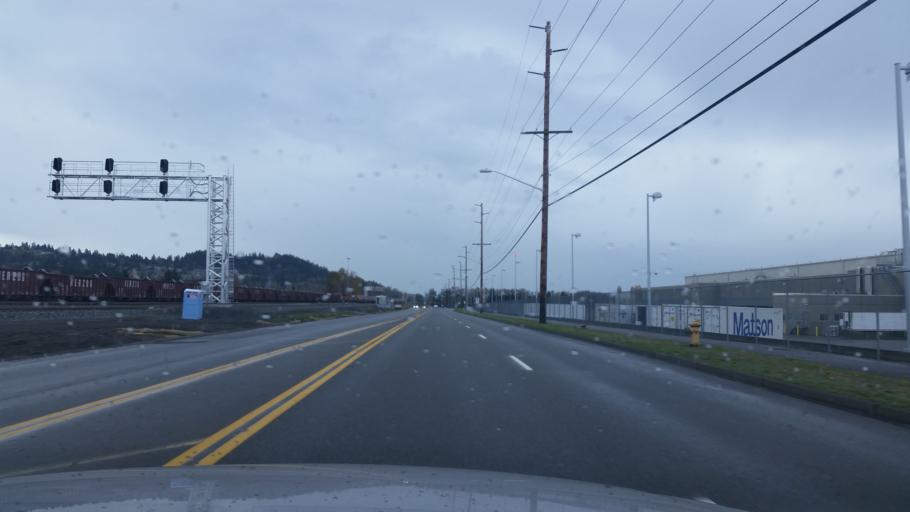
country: US
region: Washington
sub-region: King County
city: Algona
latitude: 47.2796
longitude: -122.2312
